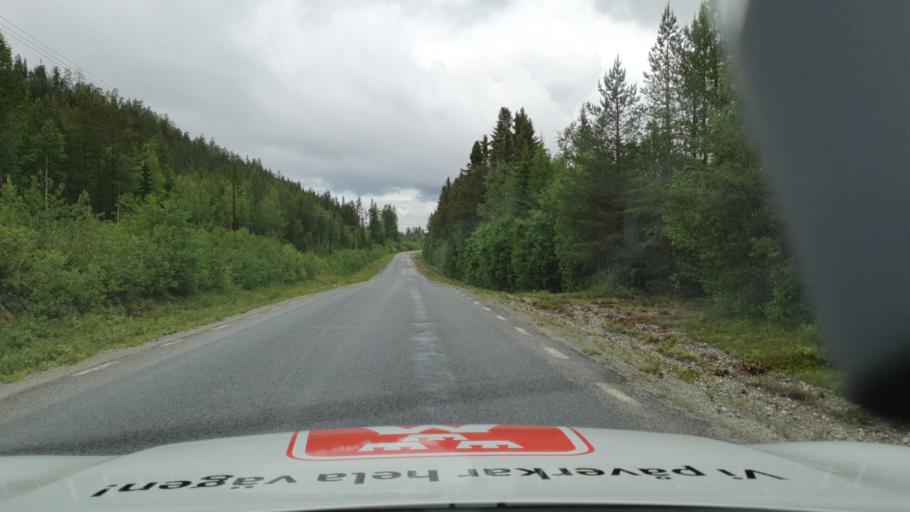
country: SE
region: Vaesterbotten
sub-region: Dorotea Kommun
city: Dorotea
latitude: 64.1748
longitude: 16.6447
